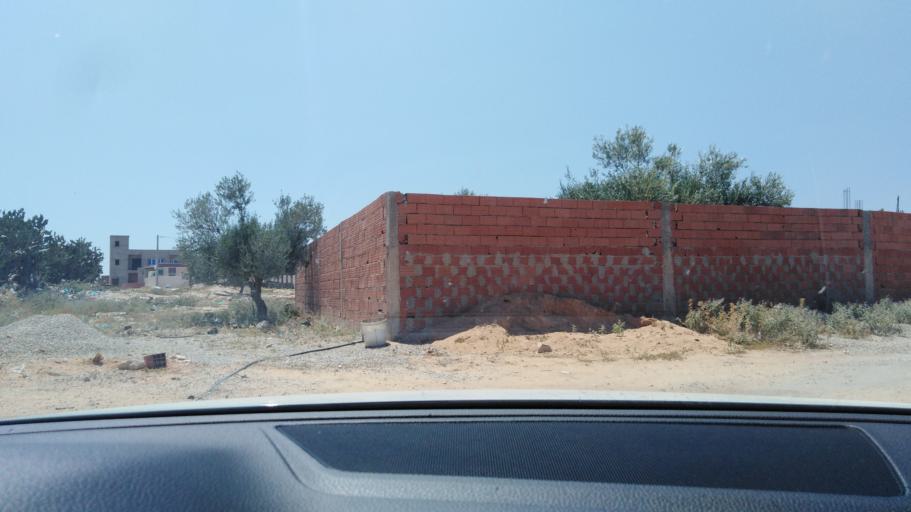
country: TN
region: Al Qayrawan
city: Sbikha
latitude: 36.1161
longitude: 10.1001
